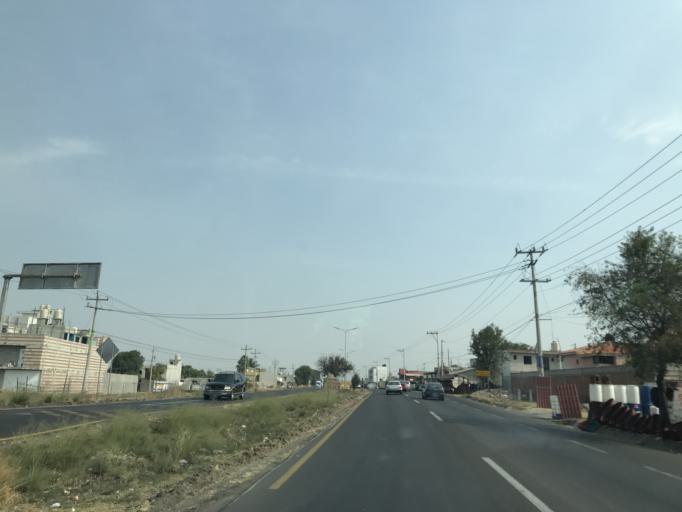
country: MX
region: Tlaxcala
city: Tenancingo
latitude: 19.1424
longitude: -98.1912
